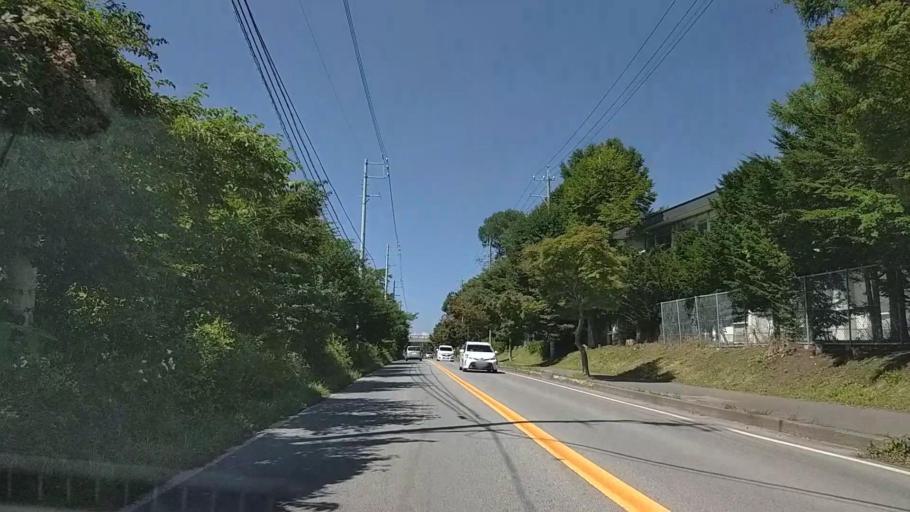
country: JP
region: Nagano
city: Saku
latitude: 36.3437
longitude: 138.6177
